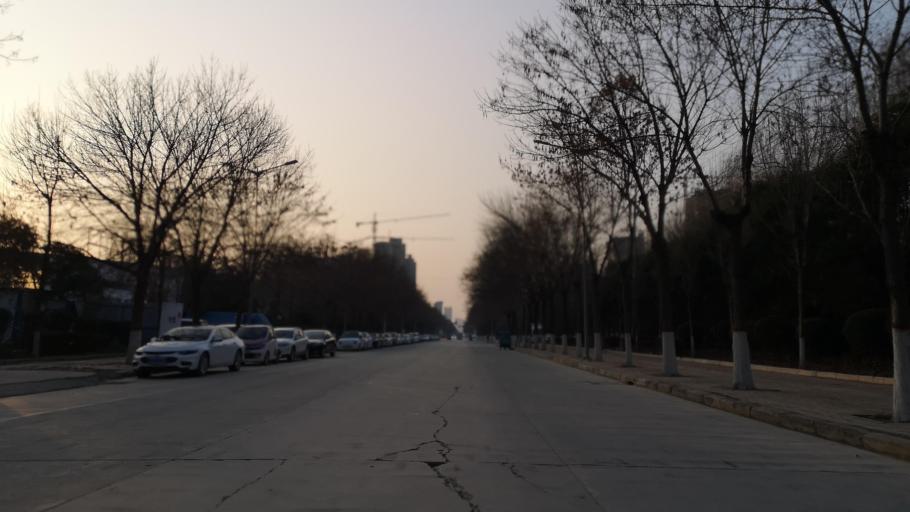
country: CN
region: Henan Sheng
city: Puyang Chengguanzhen
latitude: 35.7235
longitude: 115.0535
